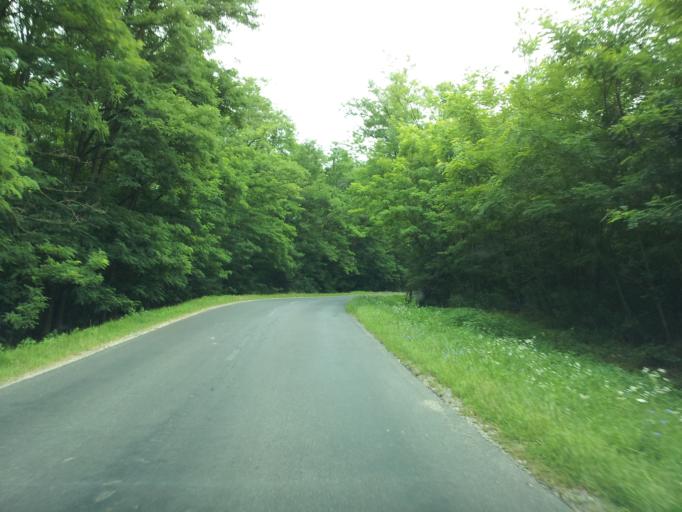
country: HU
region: Vas
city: Vasvar
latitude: 47.0409
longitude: 16.9081
